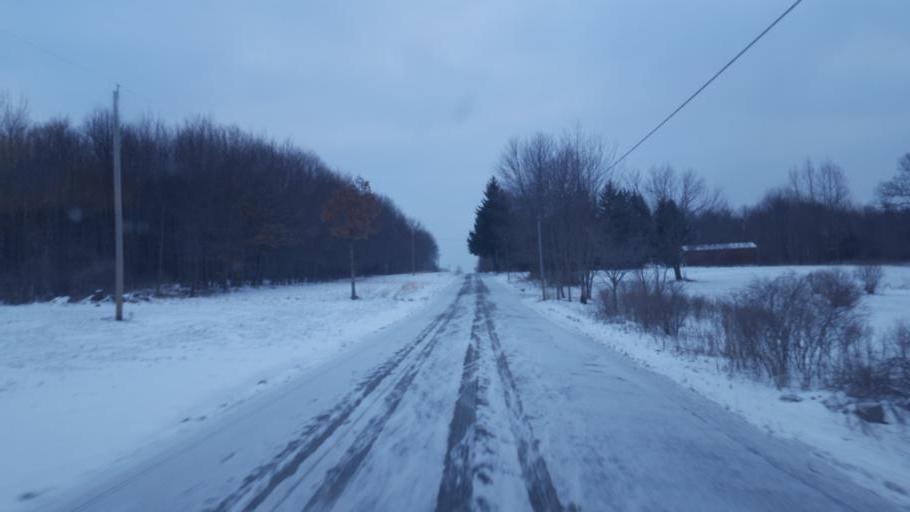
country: US
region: Pennsylvania
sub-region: Crawford County
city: Cochranton
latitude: 41.4333
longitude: -79.9978
